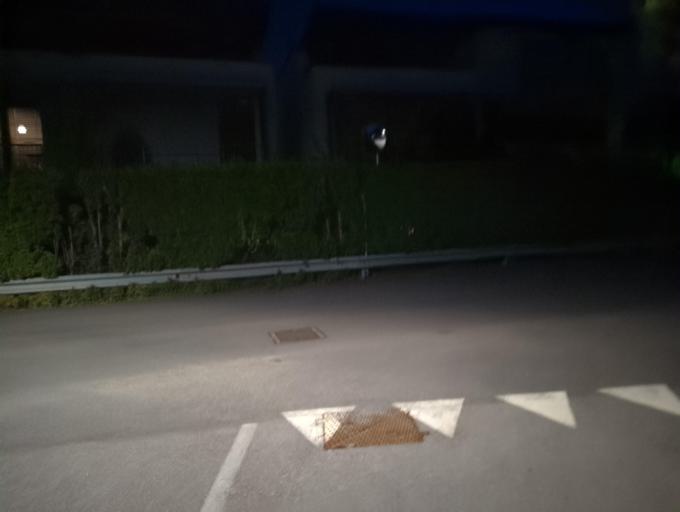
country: IT
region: Trentino-Alto Adige
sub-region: Bolzano
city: Andriano
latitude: 46.5211
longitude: 11.2309
